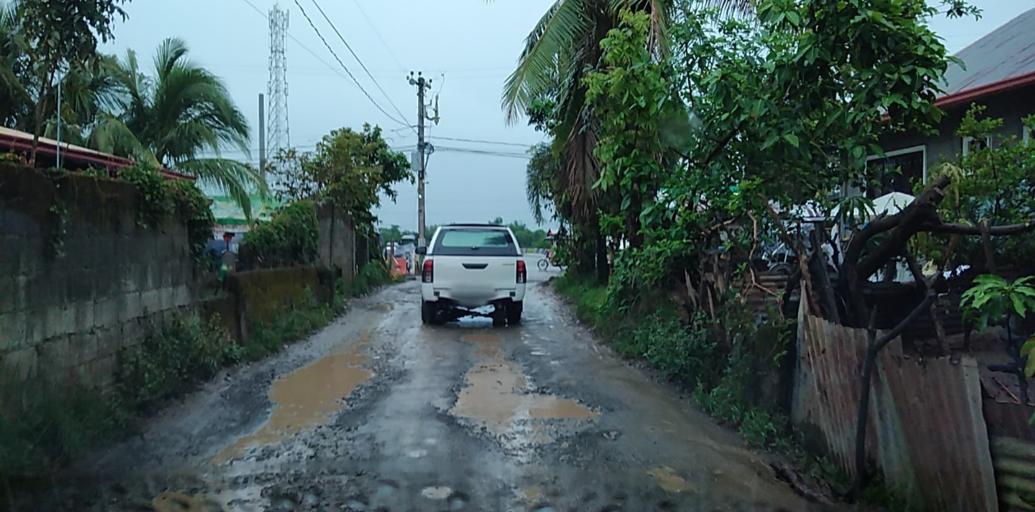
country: PH
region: Central Luzon
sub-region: Province of Pampanga
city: Batasan Bata
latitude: 15.1408
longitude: 120.9452
